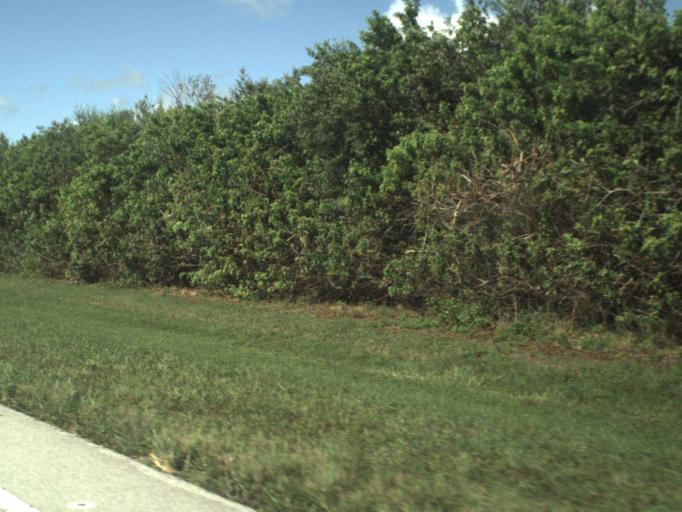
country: US
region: Florida
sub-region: Indian River County
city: Vero Beach
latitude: 27.6553
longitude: -80.3843
